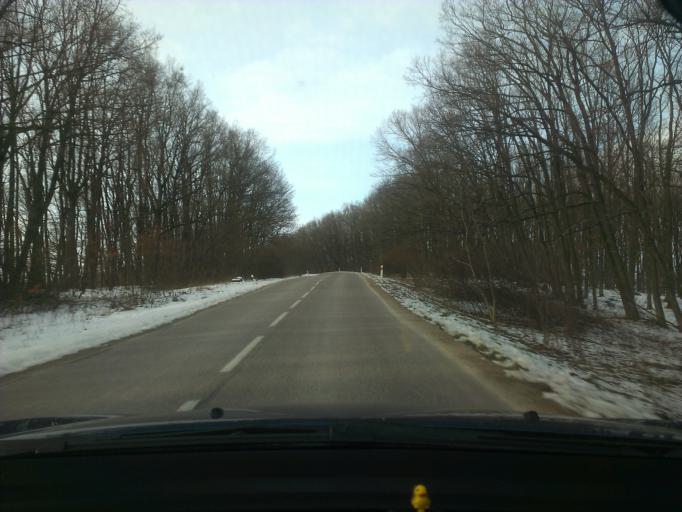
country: SK
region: Nitriansky
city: Stara Tura
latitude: 48.7219
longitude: 17.6820
